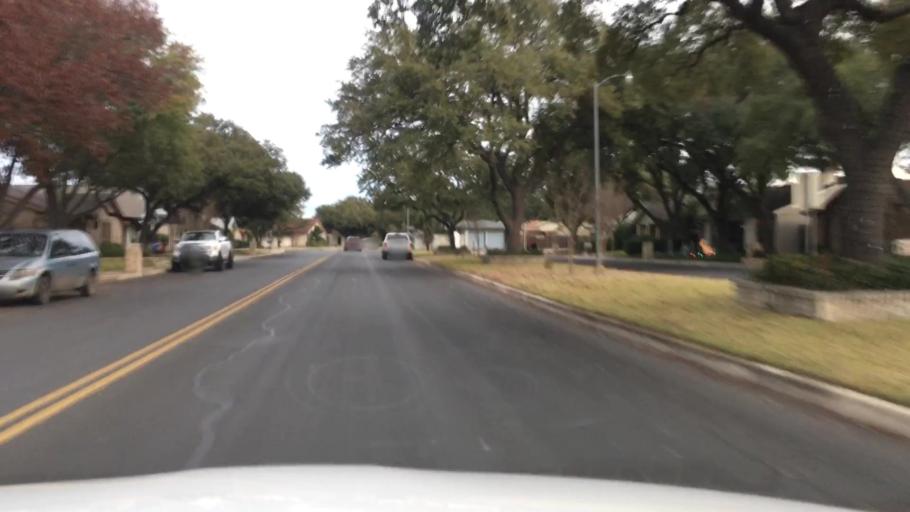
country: US
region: Texas
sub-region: Bexar County
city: Windcrest
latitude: 29.5121
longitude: -98.3861
